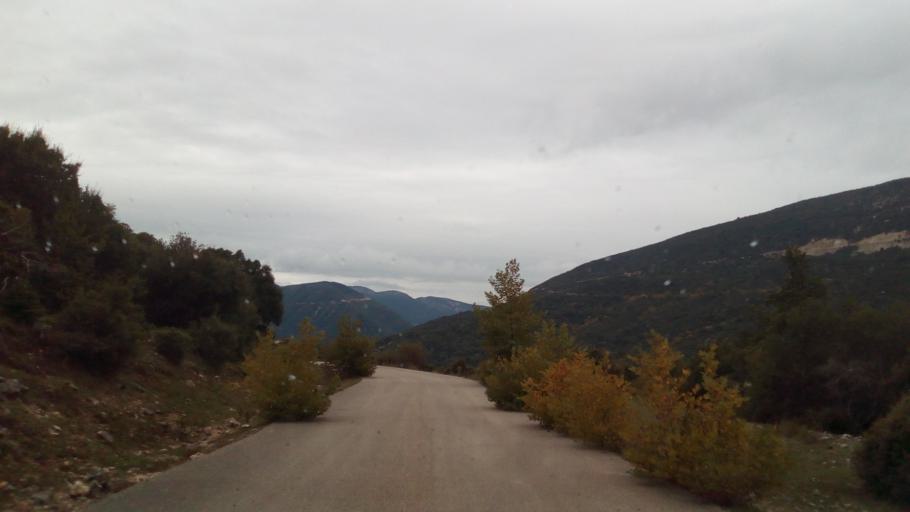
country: GR
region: West Greece
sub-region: Nomos Aitolias kai Akarnanias
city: Thermo
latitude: 38.6125
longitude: 21.8436
